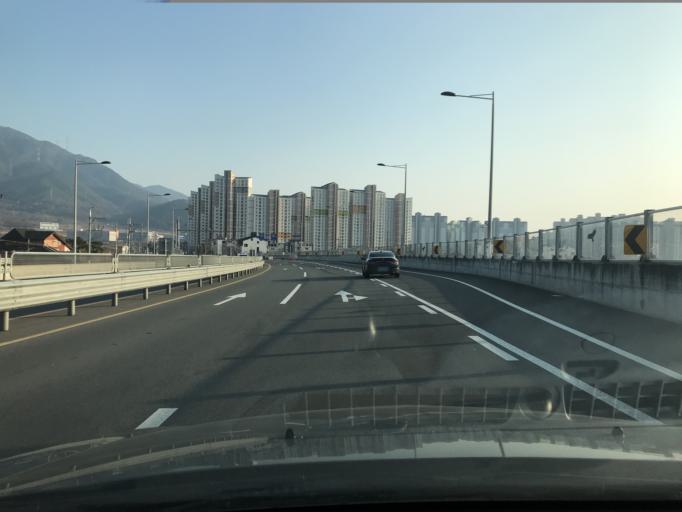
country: KR
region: Daegu
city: Hwawon
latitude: 35.7043
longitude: 128.4659
